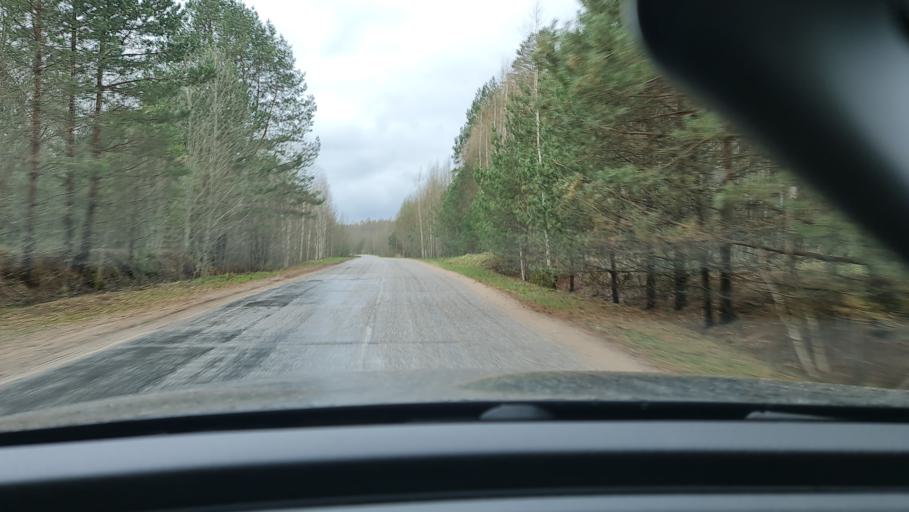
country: RU
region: Novgorod
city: Marevo
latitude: 57.1061
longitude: 31.7672
